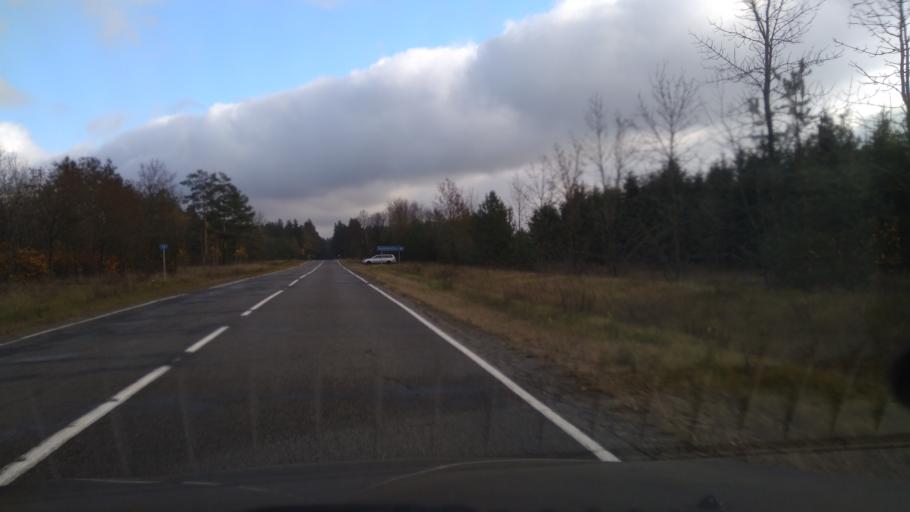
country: BY
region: Minsk
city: Slutsk
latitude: 53.2288
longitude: 27.7216
